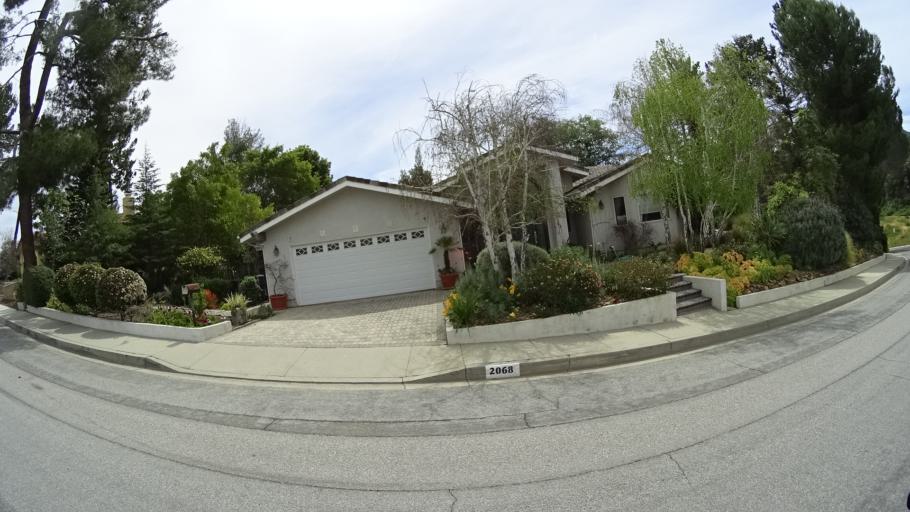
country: US
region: California
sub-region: Ventura County
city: Thousand Oaks
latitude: 34.1398
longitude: -118.8409
